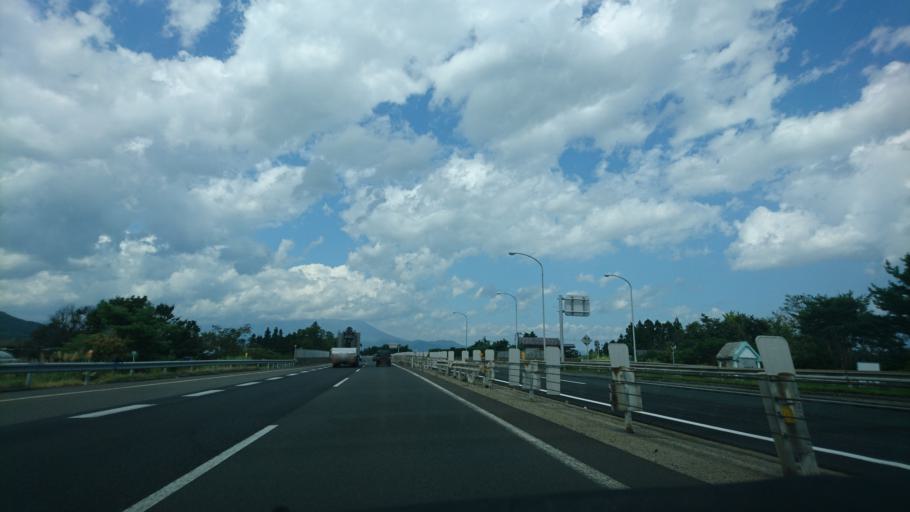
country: JP
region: Iwate
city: Morioka-shi
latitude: 39.6531
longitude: 141.1222
